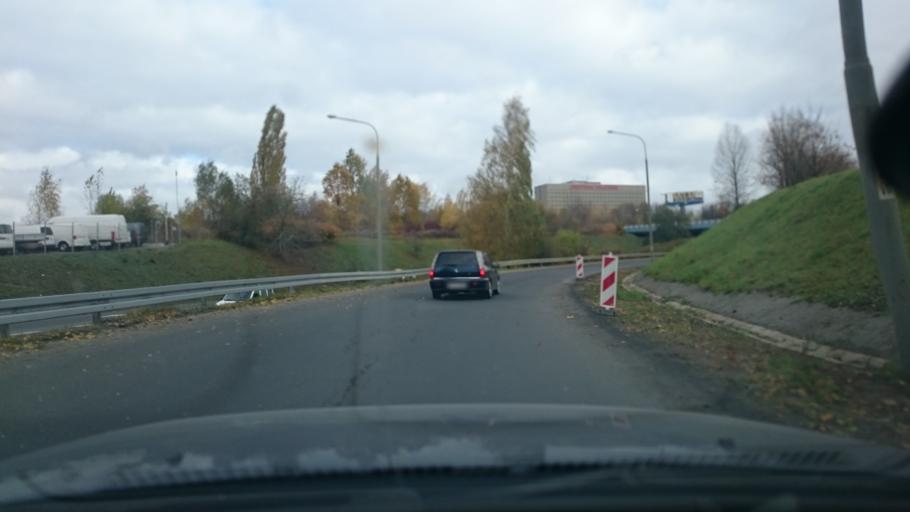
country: PL
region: Silesian Voivodeship
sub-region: Sosnowiec
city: Sosnowiec
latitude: 50.2991
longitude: 19.1195
